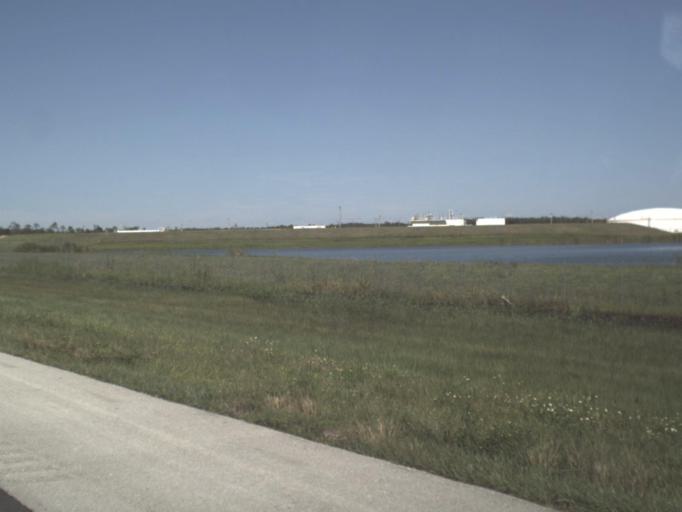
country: US
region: Florida
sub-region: Lee County
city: Bonita Springs
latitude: 26.3693
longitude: -81.7683
